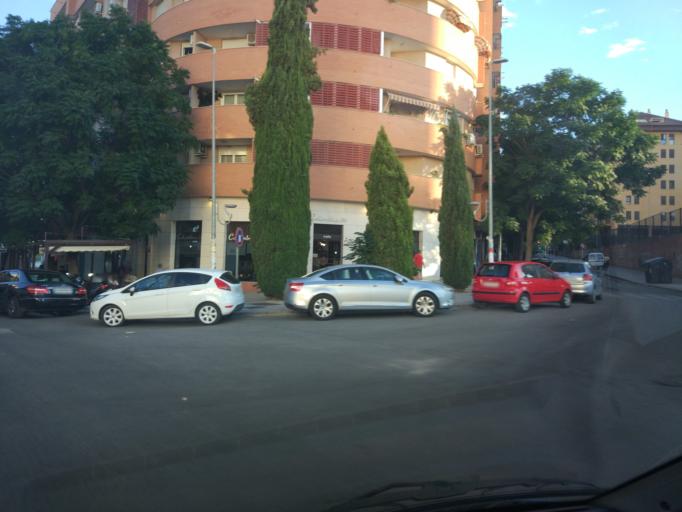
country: ES
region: Andalusia
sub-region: Provincia de Jaen
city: Jaen
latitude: 37.7864
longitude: -3.7774
